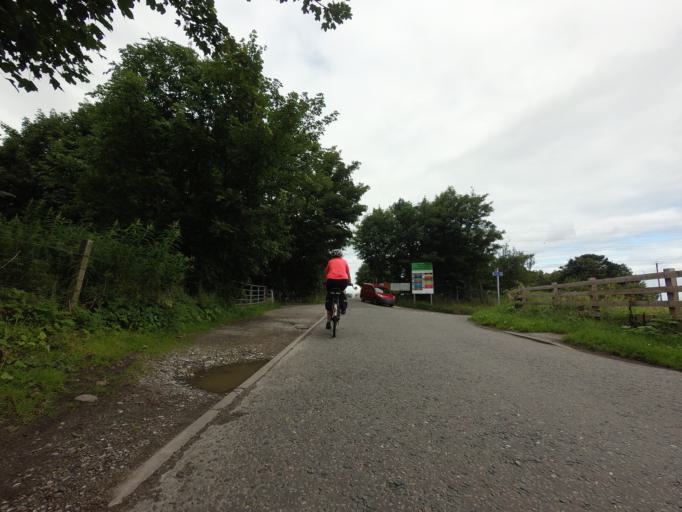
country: GB
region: Scotland
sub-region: Moray
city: Forres
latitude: 57.6155
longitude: -3.6294
